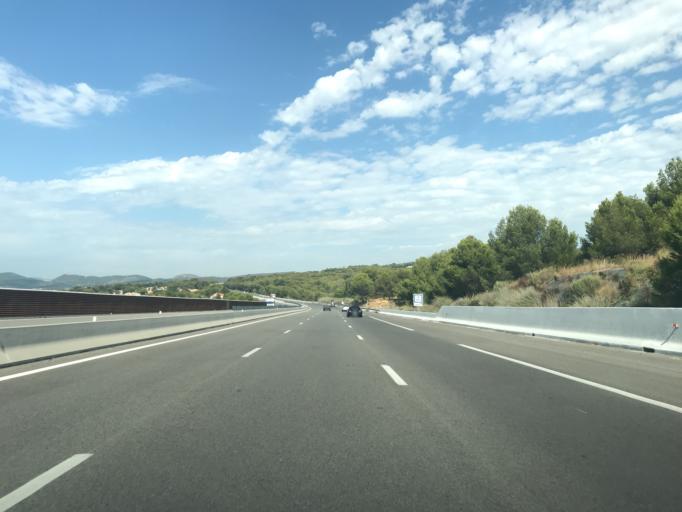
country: FR
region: Provence-Alpes-Cote d'Azur
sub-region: Departement des Bouches-du-Rhone
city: Ceyreste
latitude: 43.1930
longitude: 5.6524
